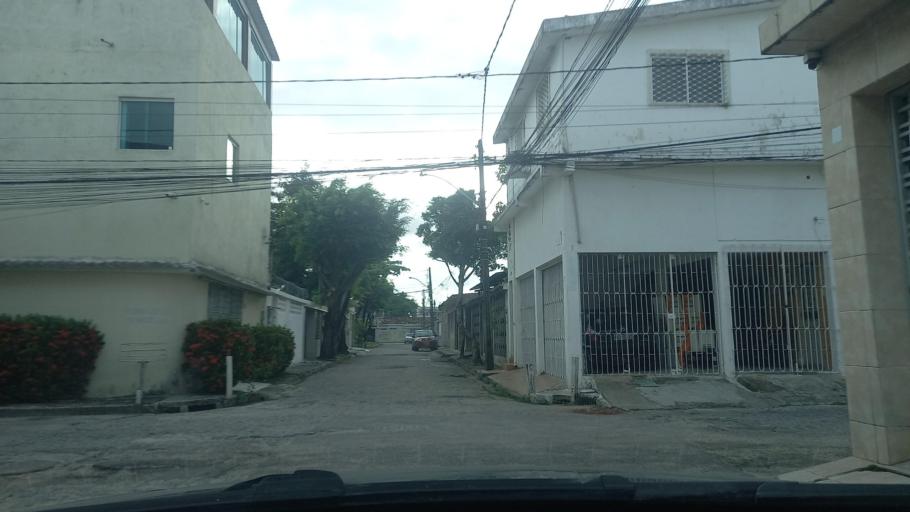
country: BR
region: Pernambuco
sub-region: Recife
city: Recife
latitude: -8.1148
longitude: -34.9190
